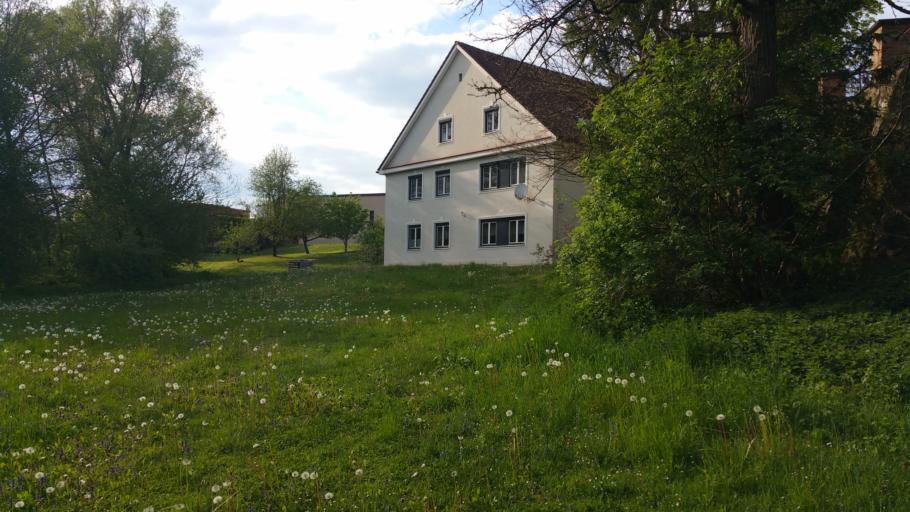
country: AT
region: Styria
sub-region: Politischer Bezirk Leibnitz
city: Gleinstatten
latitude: 46.7513
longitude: 15.3667
